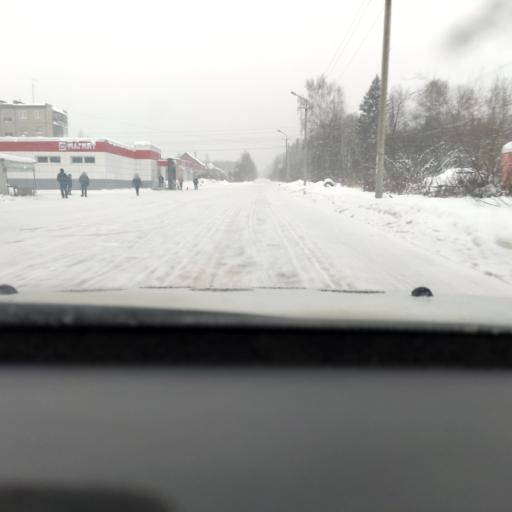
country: RU
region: Perm
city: Polazna
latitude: 58.1461
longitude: 56.4327
